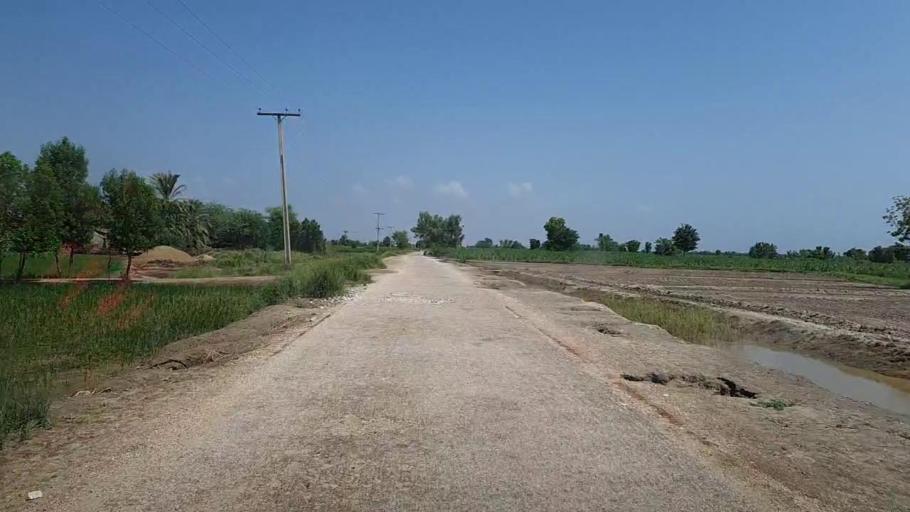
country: PK
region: Sindh
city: Bhiria
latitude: 26.8795
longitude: 68.2431
